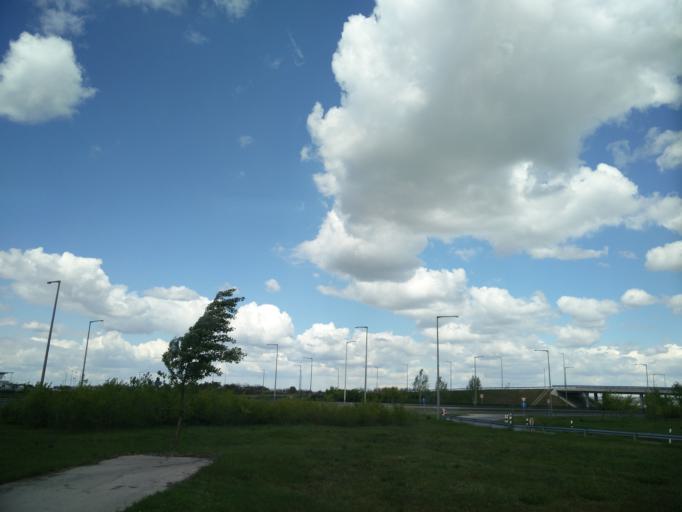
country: HU
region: Pest
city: Vecses
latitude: 47.4217
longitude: 19.2635
